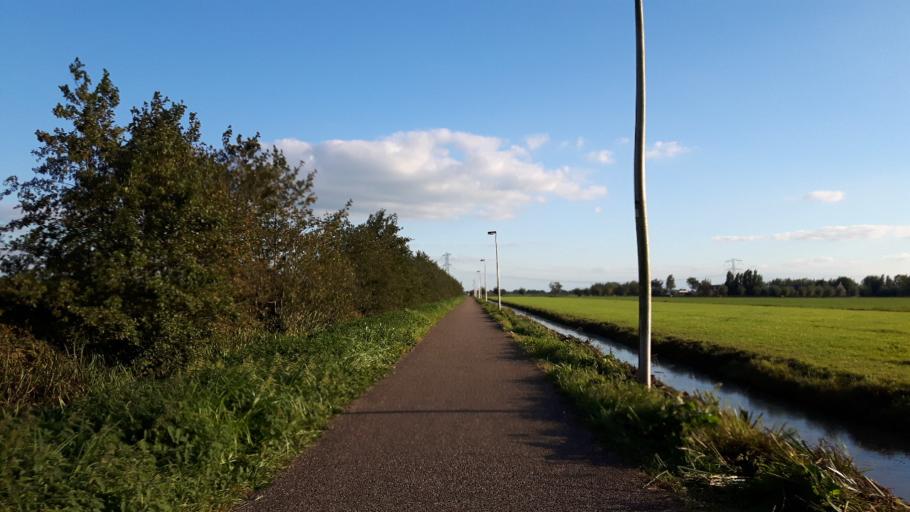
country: NL
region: Utrecht
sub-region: Gemeente Woerden
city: Woerden
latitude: 52.0624
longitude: 4.8688
